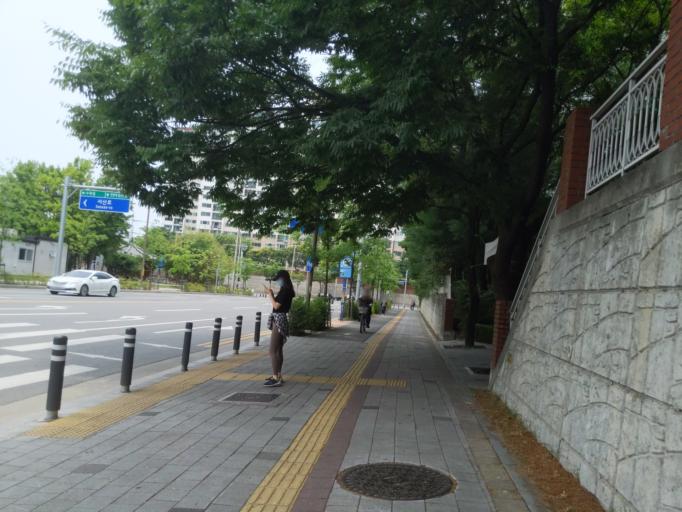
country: KR
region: Daegu
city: Hwawon
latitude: 35.8066
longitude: 128.5284
